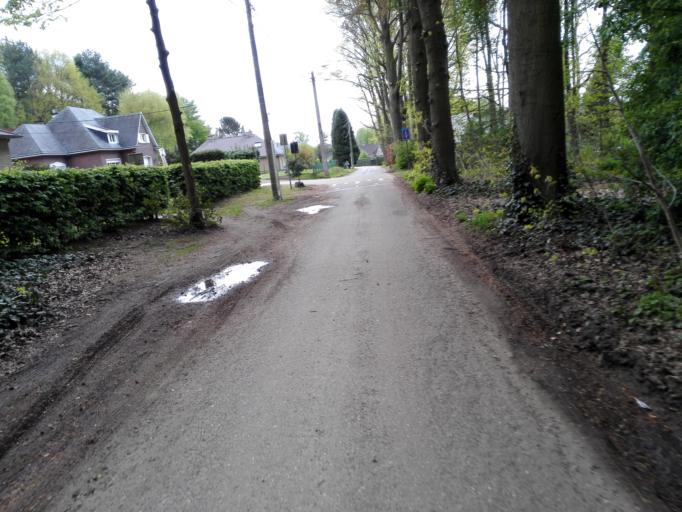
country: BE
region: Flanders
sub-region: Provincie Vlaams-Brabant
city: Rotselaar
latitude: 50.9630
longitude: 4.7413
